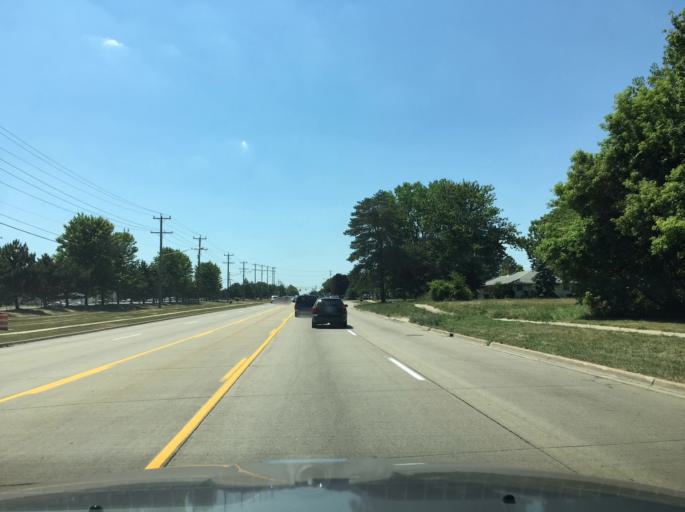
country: US
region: Michigan
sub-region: Macomb County
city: Clinton
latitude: 42.5545
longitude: -82.9055
